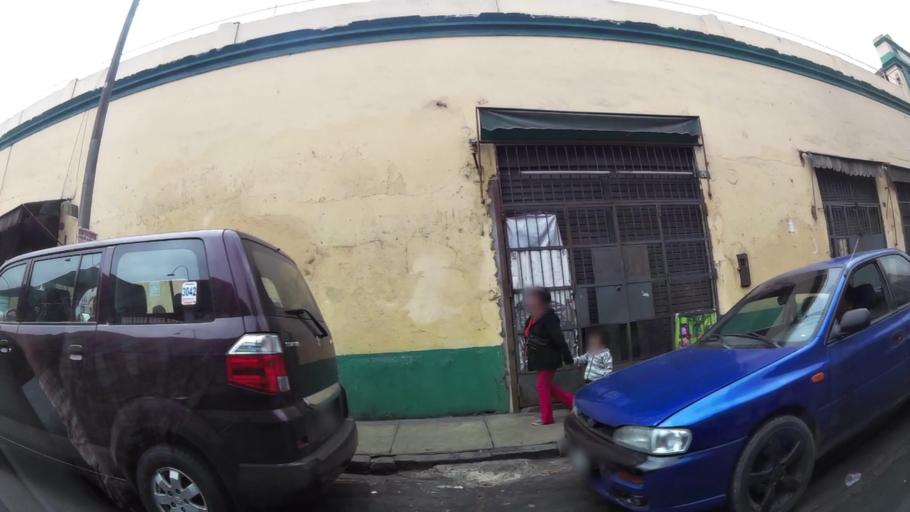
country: PE
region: Lima
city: Lima
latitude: -12.0449
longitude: -77.0392
